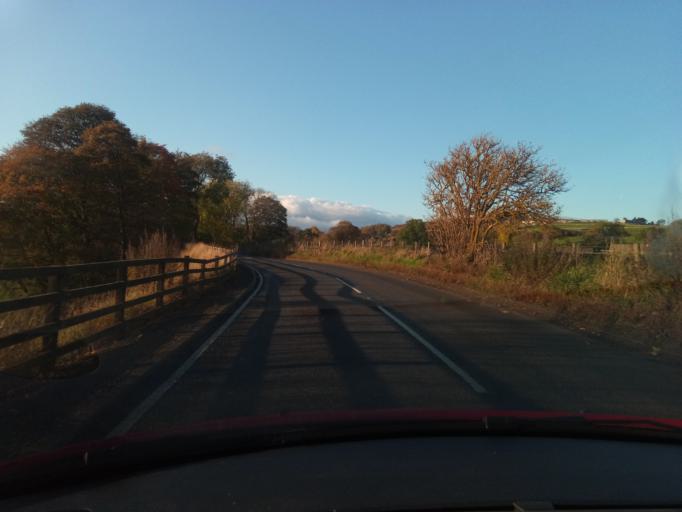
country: GB
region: England
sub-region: County Durham
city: Stanhope
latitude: 54.7392
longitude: -1.9936
